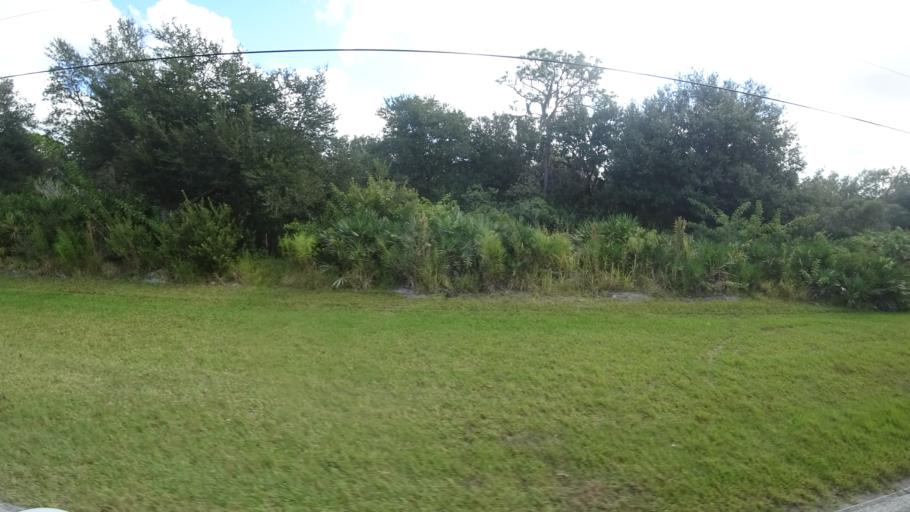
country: US
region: Florida
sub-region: Sarasota County
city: Lake Sarasota
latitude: 27.3970
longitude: -82.2711
